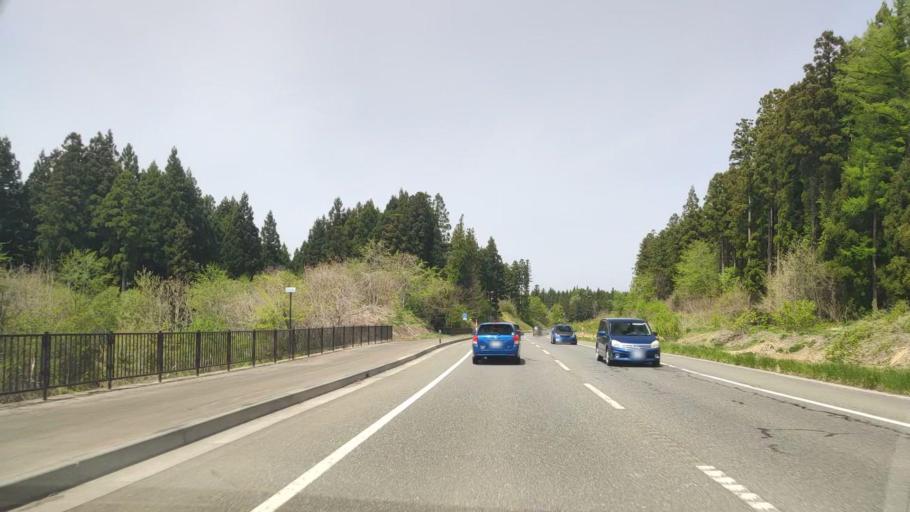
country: JP
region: Aomori
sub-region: Misawa Shi
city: Inuotose
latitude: 40.6868
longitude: 141.1697
